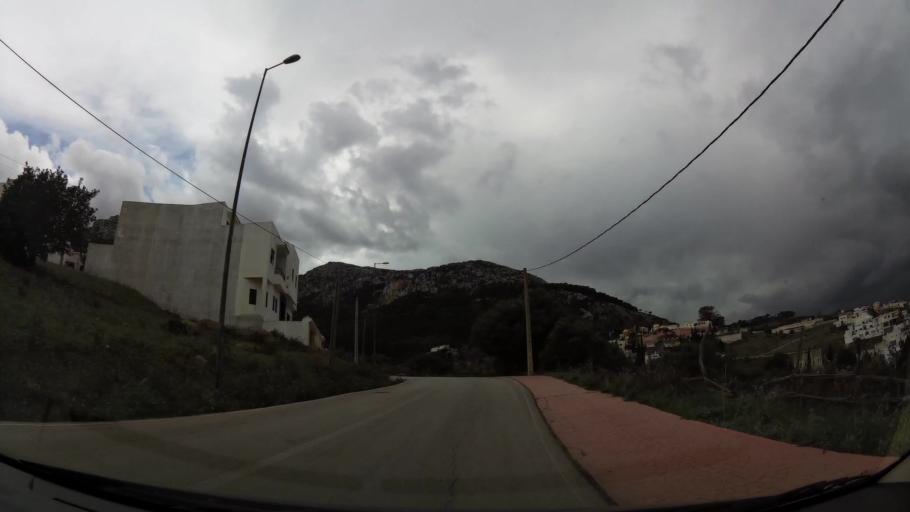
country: MA
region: Tanger-Tetouan
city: Tetouan
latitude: 35.5504
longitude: -5.3689
